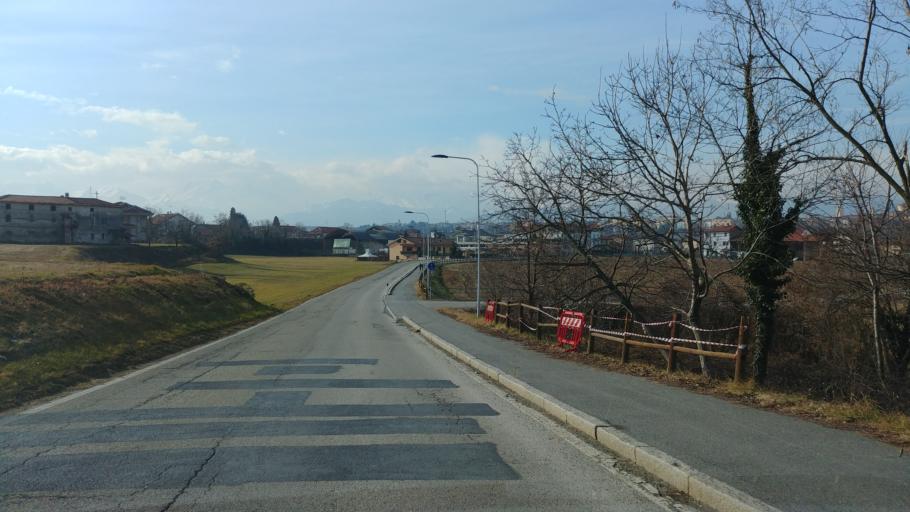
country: IT
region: Piedmont
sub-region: Provincia di Cuneo
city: Cuneo
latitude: 44.3943
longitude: 7.5696
